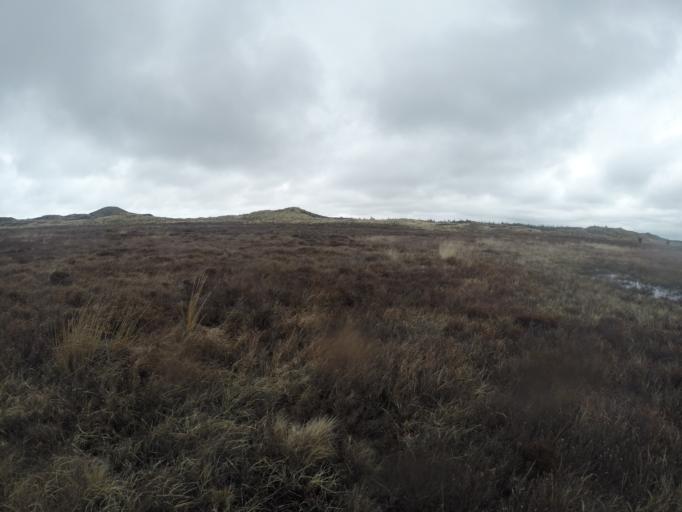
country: DK
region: North Denmark
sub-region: Thisted Kommune
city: Hurup
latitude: 56.8968
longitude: 8.3338
